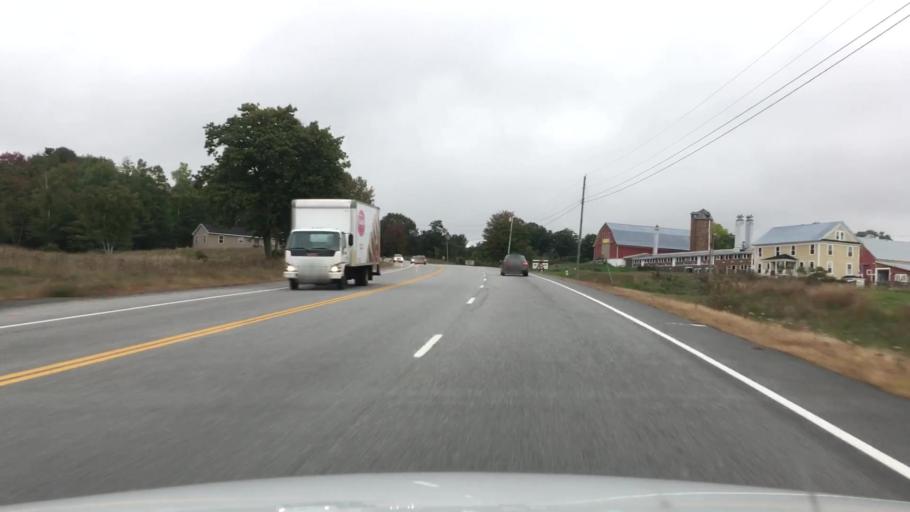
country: US
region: Maine
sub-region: Androscoggin County
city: Poland
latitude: 44.0829
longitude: -70.4184
